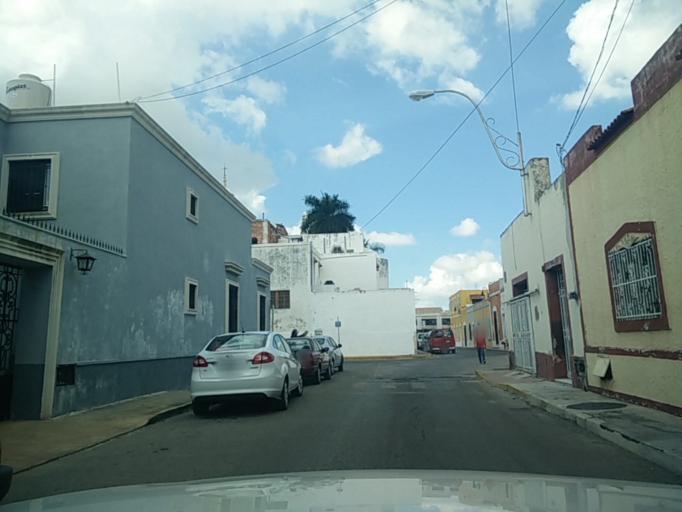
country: MX
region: Yucatan
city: Merida
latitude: 20.9766
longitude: -89.6203
